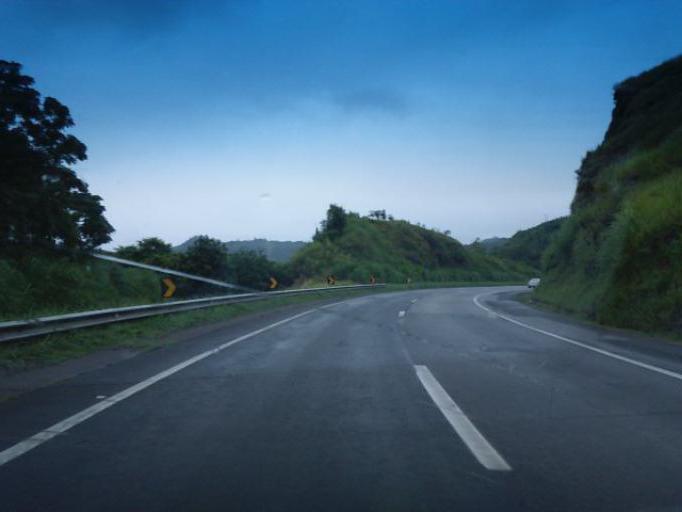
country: BR
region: Sao Paulo
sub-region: Cajati
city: Cajati
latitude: -24.7989
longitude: -48.2113
